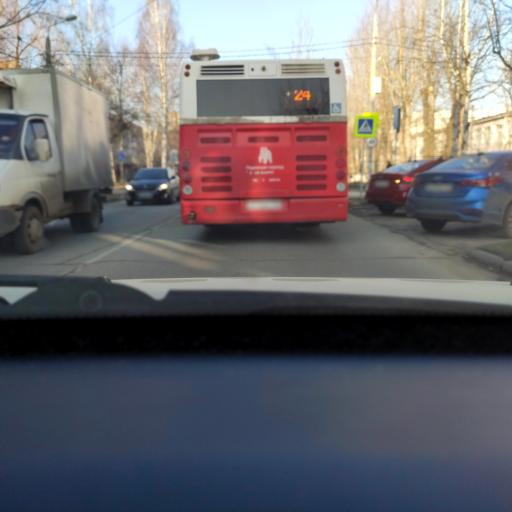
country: RU
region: Perm
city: Perm
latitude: 58.1050
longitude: 56.3843
